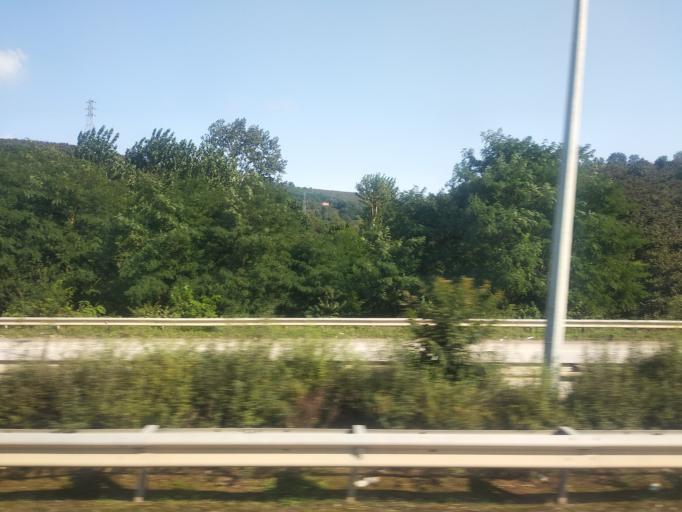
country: TR
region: Ordu
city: Ordu
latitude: 40.9950
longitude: 37.8180
